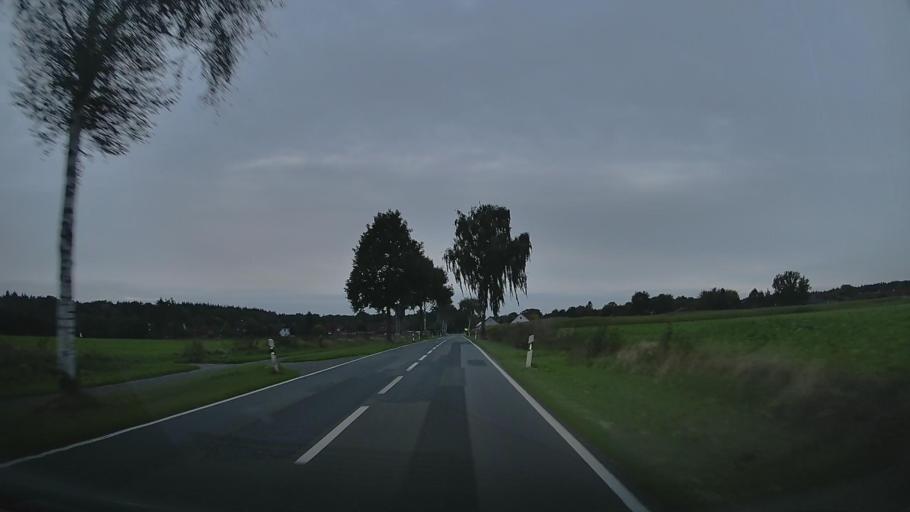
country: DE
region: Lower Saxony
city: Wildeshausen
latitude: 52.9003
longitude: 8.4780
